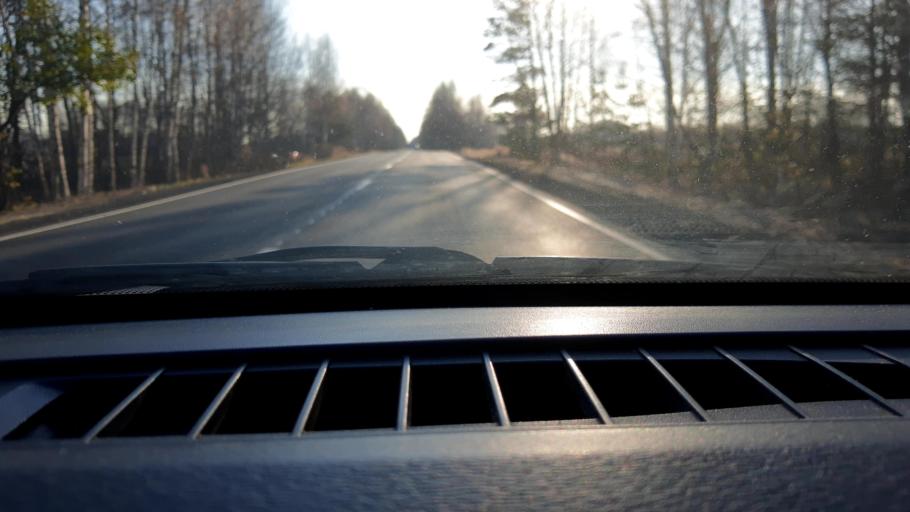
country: RU
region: Nizjnij Novgorod
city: Novaya Balakhna
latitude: 56.5583
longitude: 43.7343
